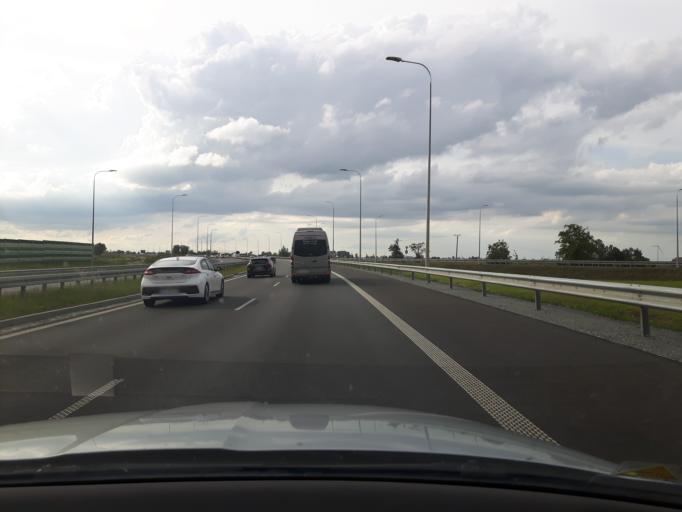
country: PL
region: Pomeranian Voivodeship
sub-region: Powiat nowodworski
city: Nowy Dwor Gdanski
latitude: 54.2133
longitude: 19.1024
